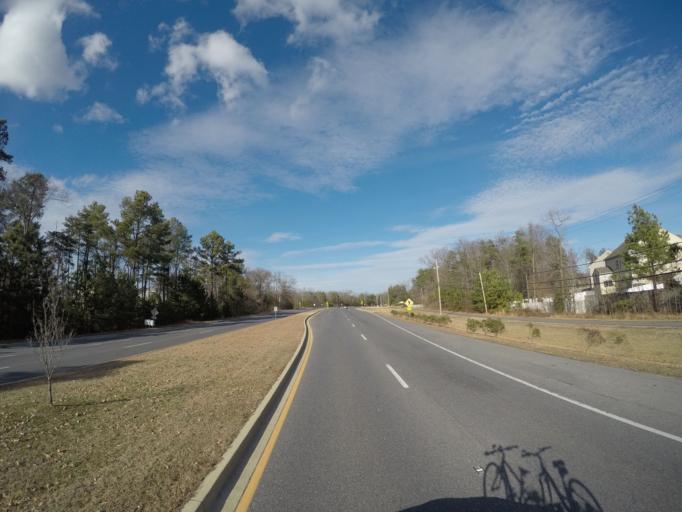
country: US
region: Maryland
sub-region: Charles County
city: Waldorf
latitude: 38.6263
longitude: -76.9683
